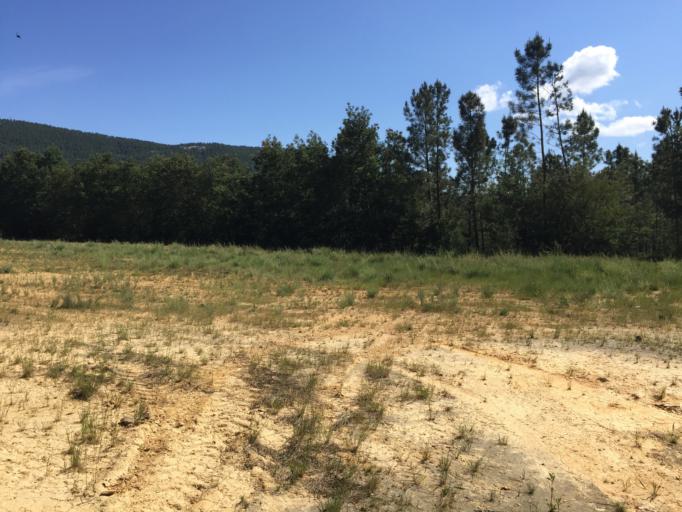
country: PT
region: Coimbra
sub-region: Pampilhosa da Serra
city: Pampilhosa da Serra
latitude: 40.0811
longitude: -7.7775
